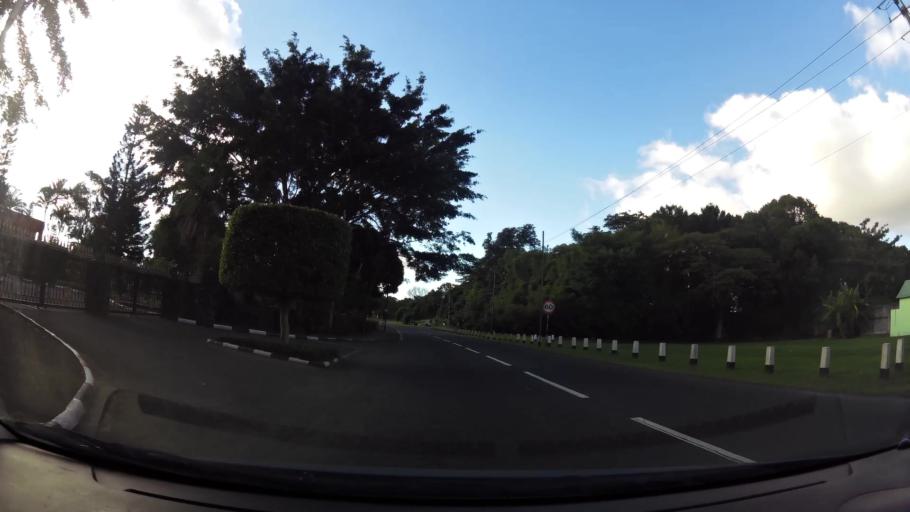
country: MU
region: Plaines Wilhems
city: Vacoas
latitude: -20.2837
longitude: 57.4977
